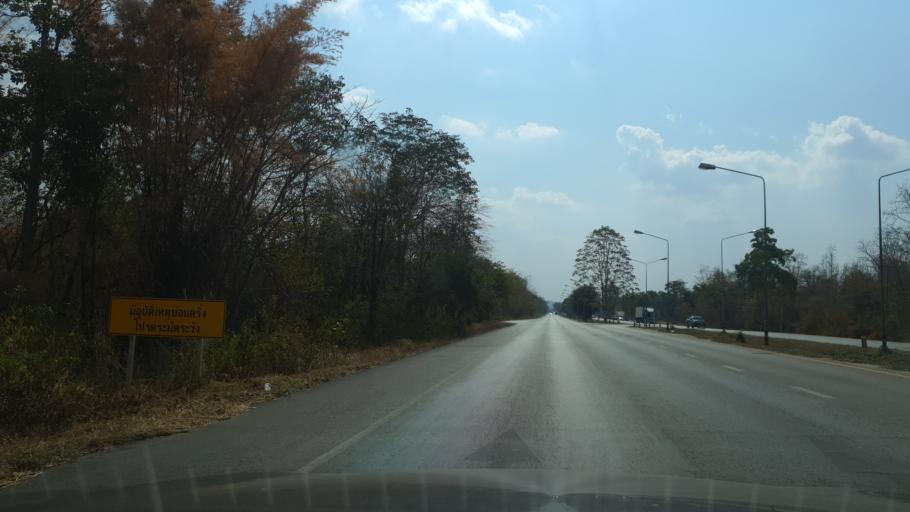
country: TH
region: Lampang
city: Mae Phrik
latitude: 17.4412
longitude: 99.1591
